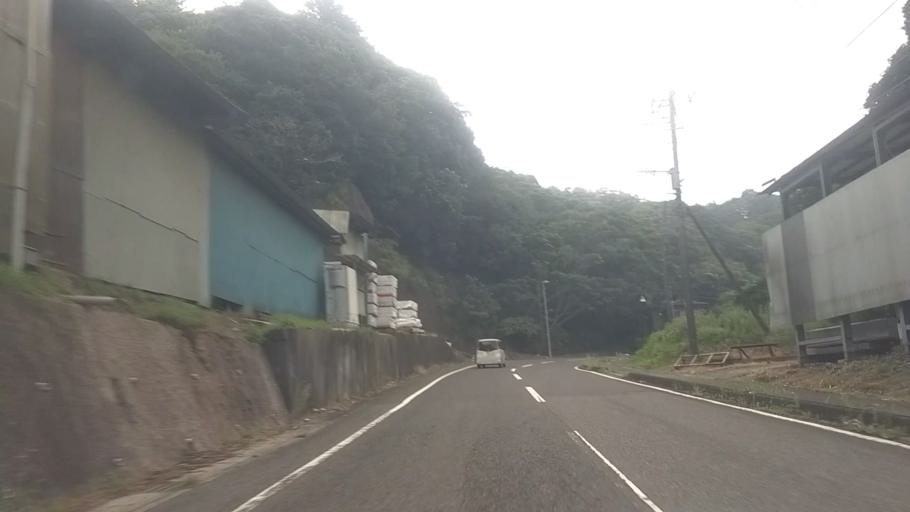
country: JP
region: Chiba
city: Kawaguchi
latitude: 35.2439
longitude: 140.1726
